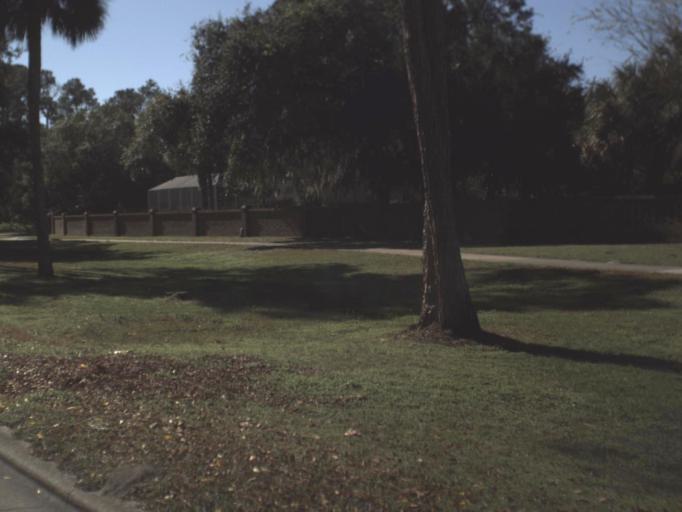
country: US
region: Florida
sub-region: Flagler County
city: Palm Coast
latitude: 29.5667
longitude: -81.1916
